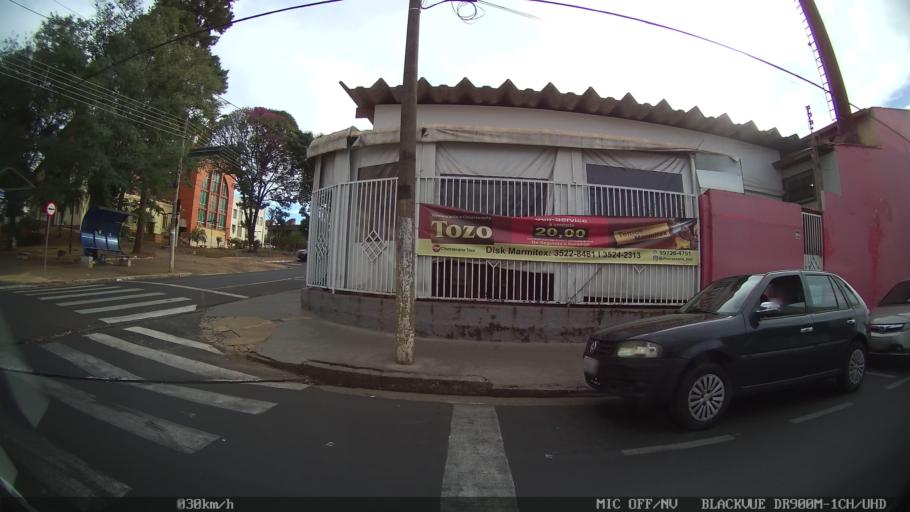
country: BR
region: Sao Paulo
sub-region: Catanduva
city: Catanduva
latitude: -21.1293
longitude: -48.9691
